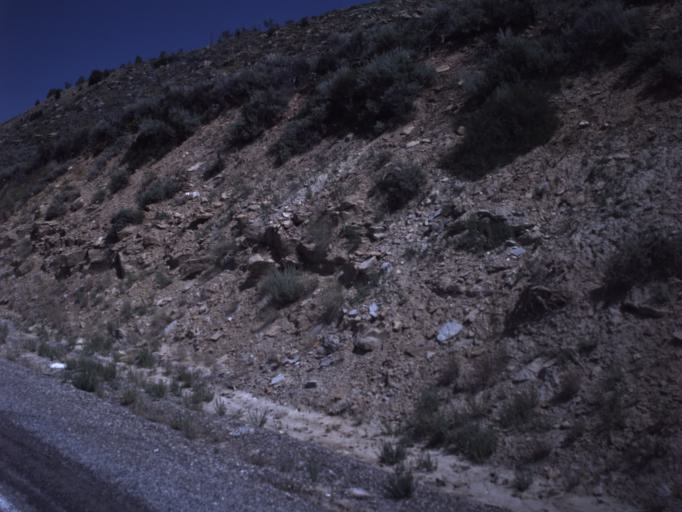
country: US
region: Utah
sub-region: Carbon County
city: Helper
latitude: 39.8239
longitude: -111.1362
